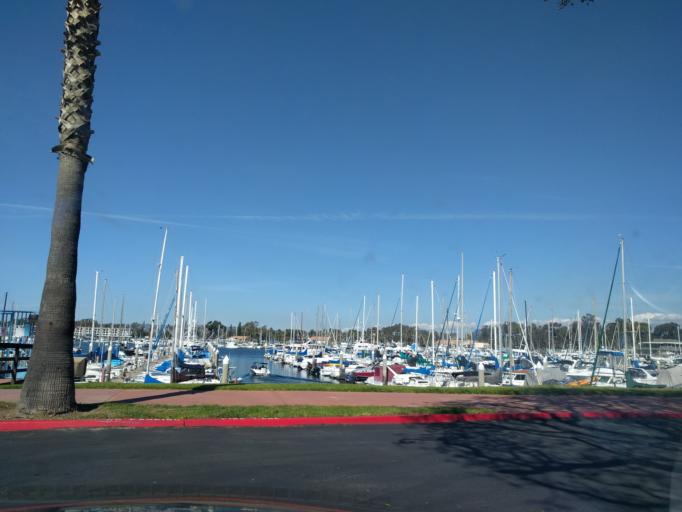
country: US
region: California
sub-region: San Diego County
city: San Diego
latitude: 32.7597
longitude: -117.2370
